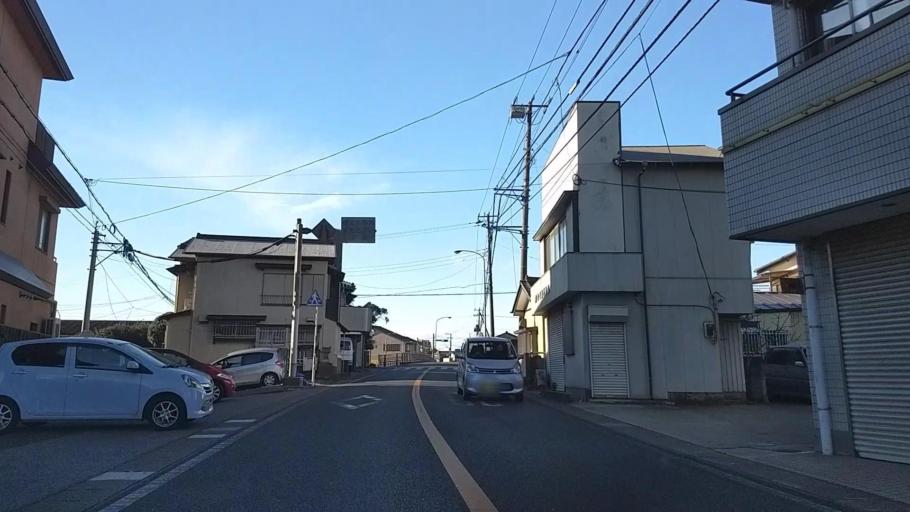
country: JP
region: Chiba
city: Kimitsu
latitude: 35.3398
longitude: 139.8657
